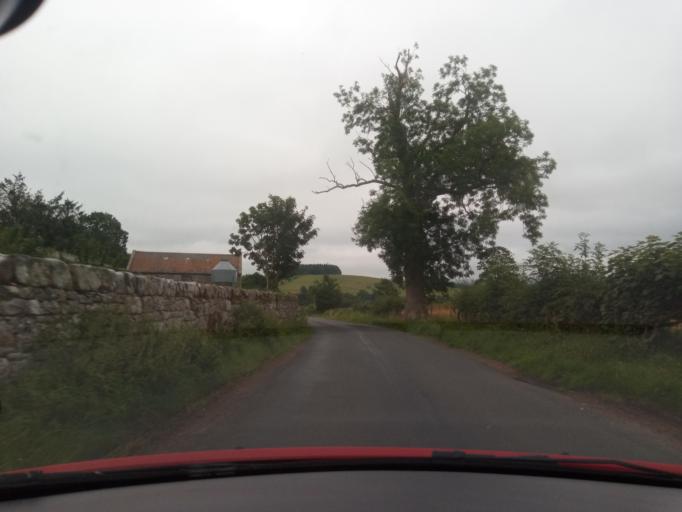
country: GB
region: England
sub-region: Northumberland
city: Otterburn
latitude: 55.3277
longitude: -2.0795
